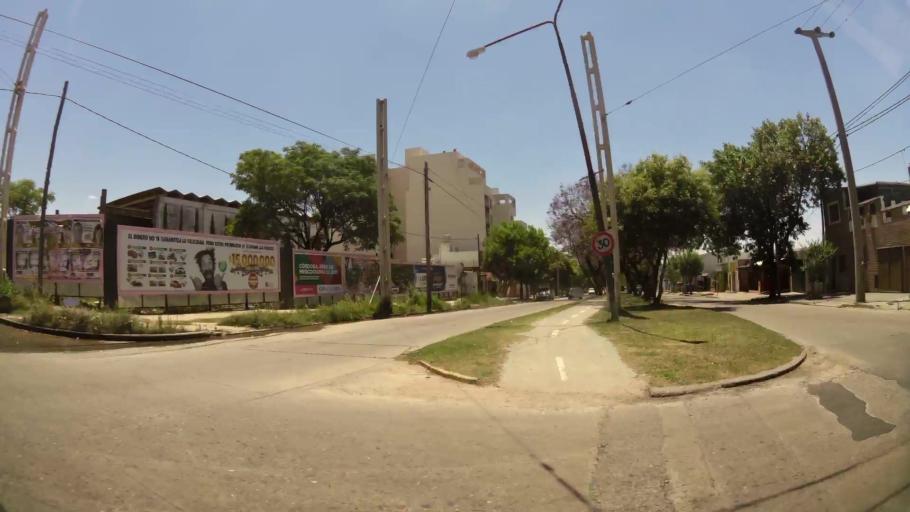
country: AR
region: Cordoba
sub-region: Departamento de Capital
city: Cordoba
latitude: -31.3999
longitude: -64.2247
